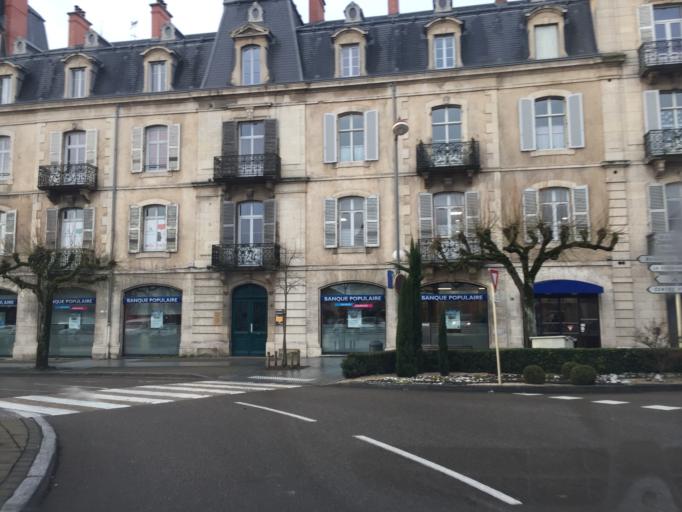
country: FR
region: Franche-Comte
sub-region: Departement du Jura
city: Dole
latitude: 47.0949
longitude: 5.4964
